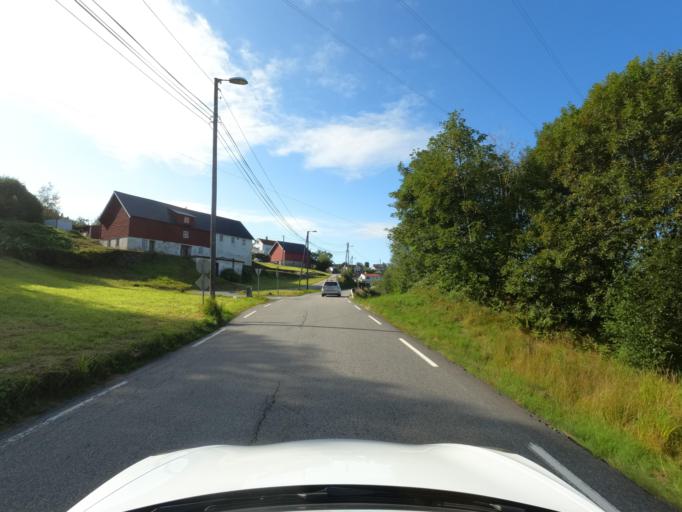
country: NO
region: Hordaland
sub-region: Bergen
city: Ytrebygda
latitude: 60.3126
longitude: 5.2602
